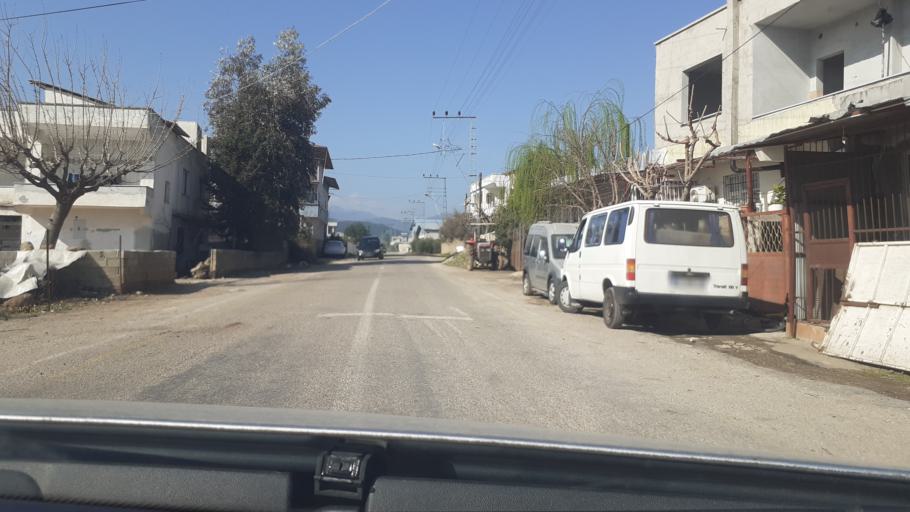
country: TR
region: Hatay
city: Aktepe
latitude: 36.7113
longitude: 36.4860
